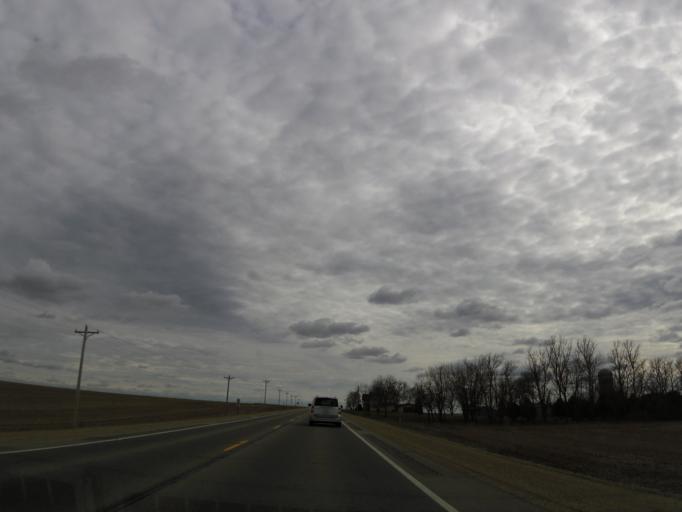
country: US
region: Iowa
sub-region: Chickasaw County
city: New Hampton
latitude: 43.1523
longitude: -92.2989
